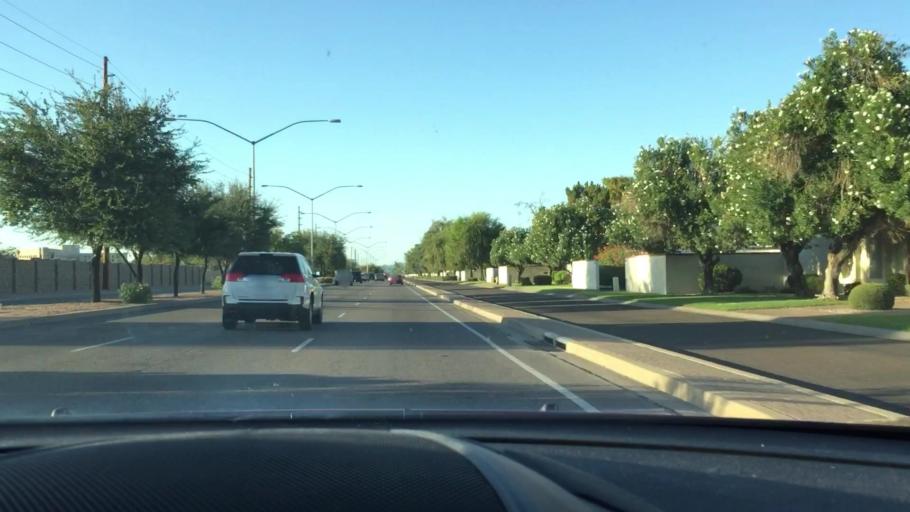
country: US
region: Arizona
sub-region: Maricopa County
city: Gilbert
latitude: 33.4027
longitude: -111.6846
